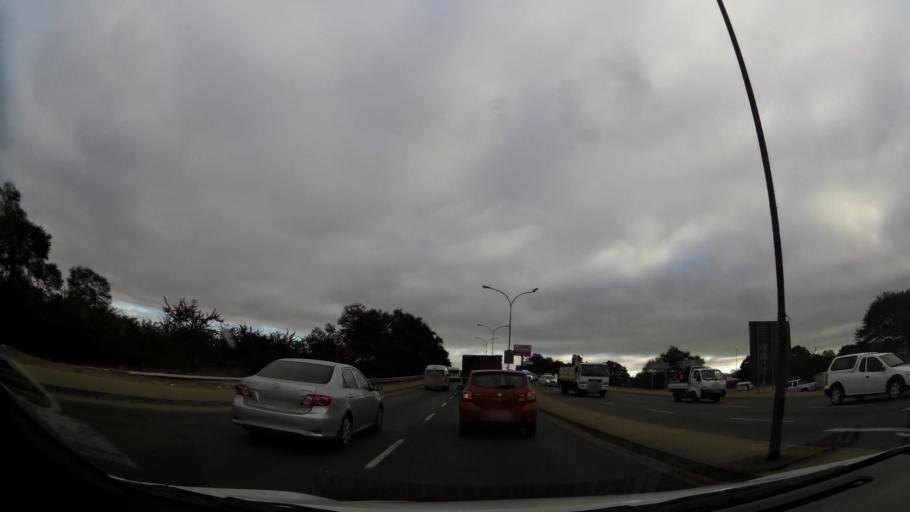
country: ZA
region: Limpopo
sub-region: Capricorn District Municipality
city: Polokwane
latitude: -23.9039
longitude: 29.4413
